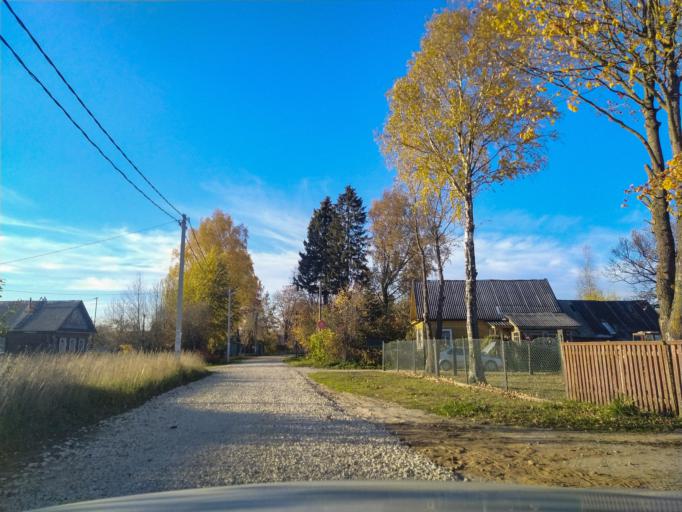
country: RU
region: Leningrad
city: Siverskiy
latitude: 59.3233
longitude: 30.0456
